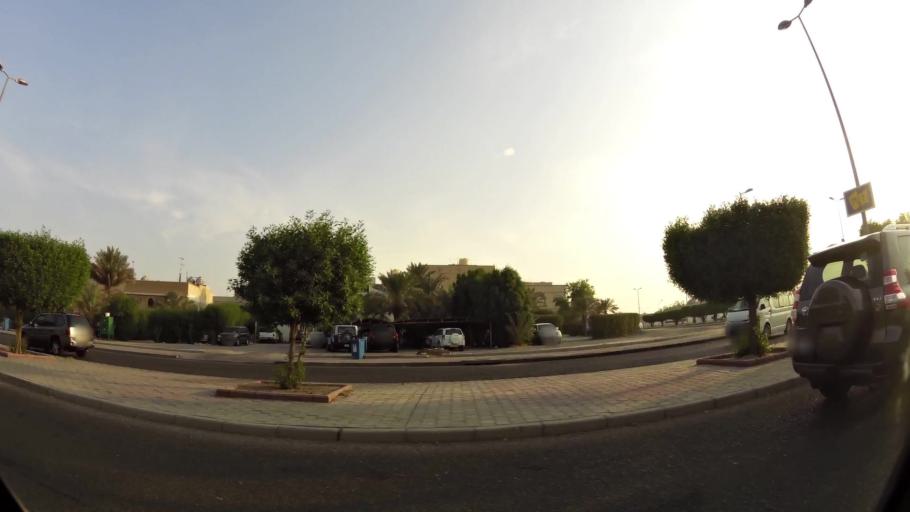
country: KW
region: Mubarak al Kabir
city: Sabah as Salim
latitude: 29.2494
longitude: 48.0767
